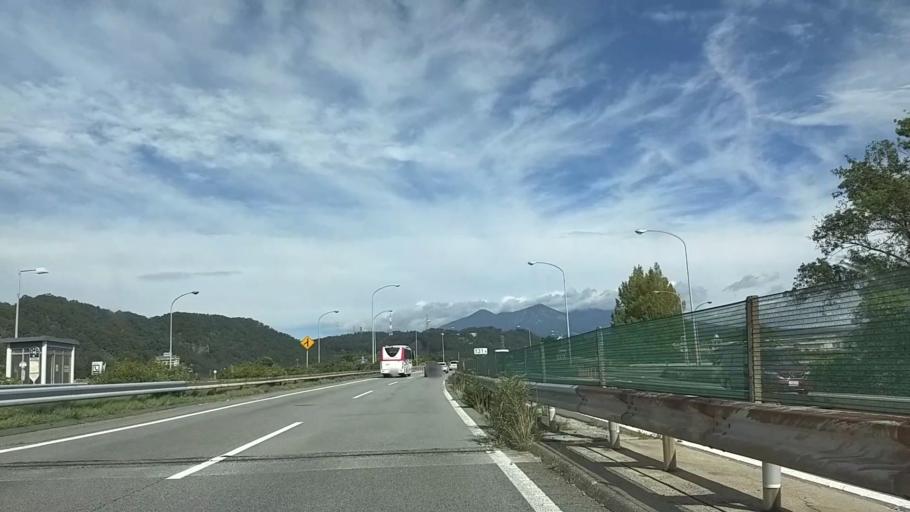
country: JP
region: Yamanashi
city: Nirasaki
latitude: 35.7723
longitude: 138.4241
